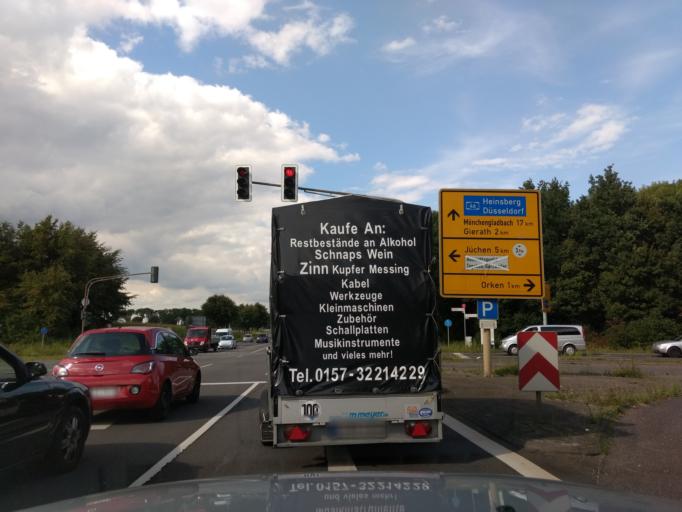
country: DE
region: North Rhine-Westphalia
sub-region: Regierungsbezirk Dusseldorf
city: Grevenbroich
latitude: 51.1012
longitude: 6.5645
